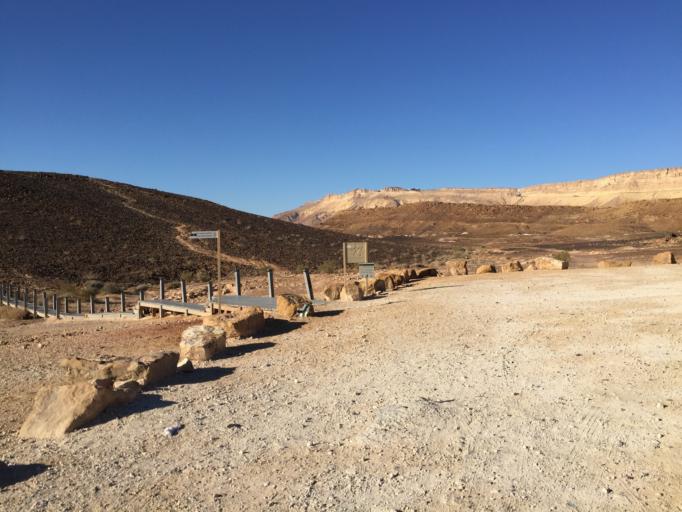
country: IL
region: Southern District
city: Mitzpe Ramon
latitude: 30.6171
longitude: 34.8403
